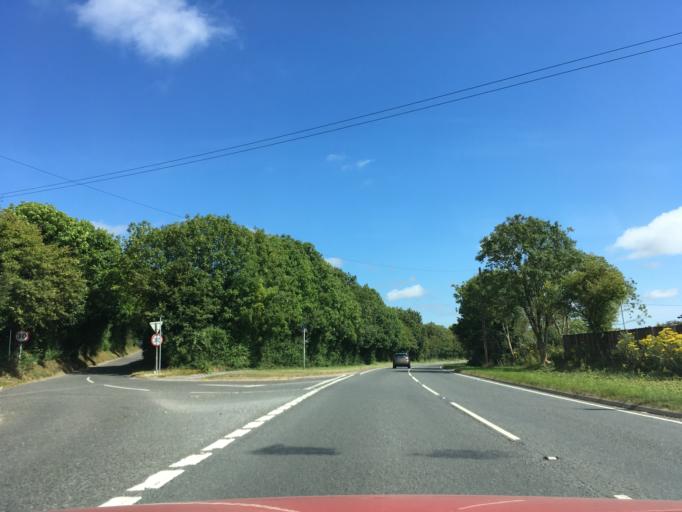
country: GB
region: England
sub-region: Dorset
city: Dorchester
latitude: 50.7339
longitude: -2.4646
